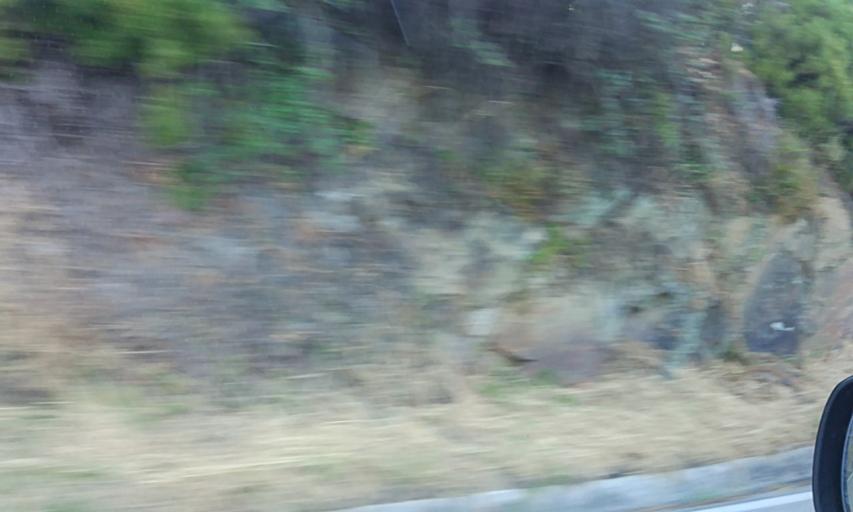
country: PT
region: Viseu
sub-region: Sao Joao da Pesqueira
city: Sao Joao da Pesqueira
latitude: 41.2449
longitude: -7.4321
